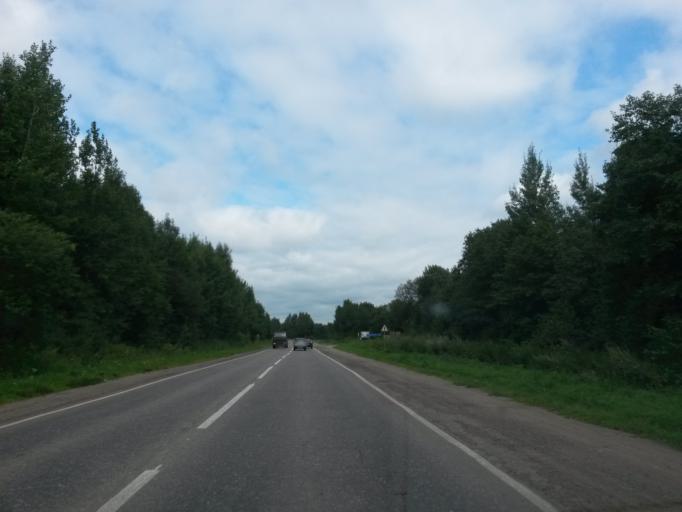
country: RU
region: Jaroslavl
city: Yaroslavl
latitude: 57.5339
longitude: 39.8730
